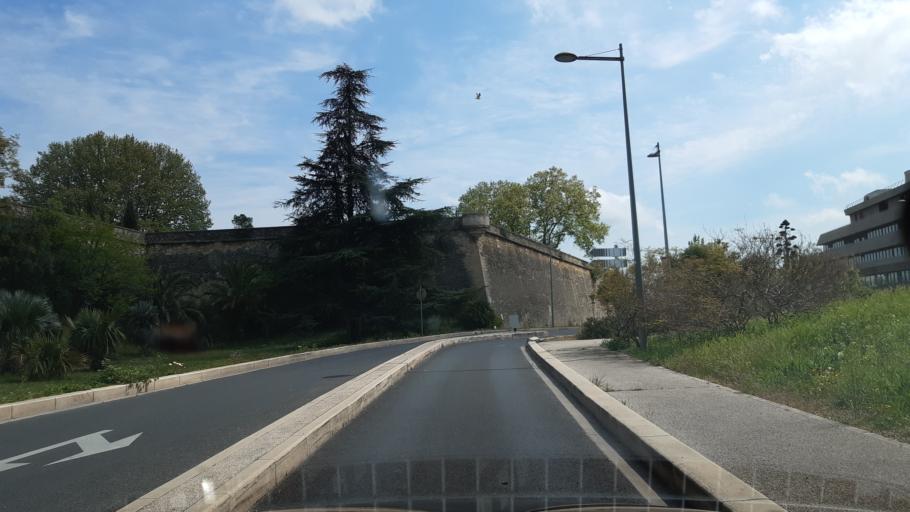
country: FR
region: Languedoc-Roussillon
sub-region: Departement de l'Herault
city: Montpellier
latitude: 43.6104
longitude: 3.8852
